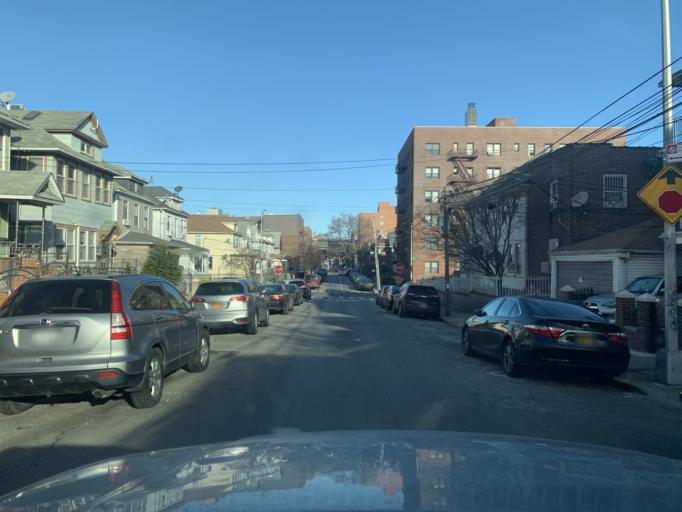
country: US
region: New York
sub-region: Queens County
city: Long Island City
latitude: 40.7446
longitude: -73.8919
